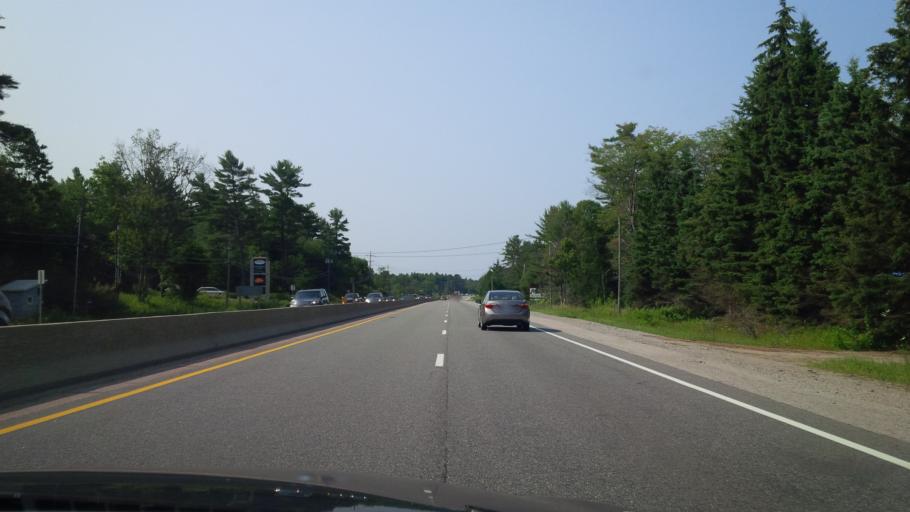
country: CA
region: Ontario
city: Gravenhurst
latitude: 44.8083
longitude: -79.3272
